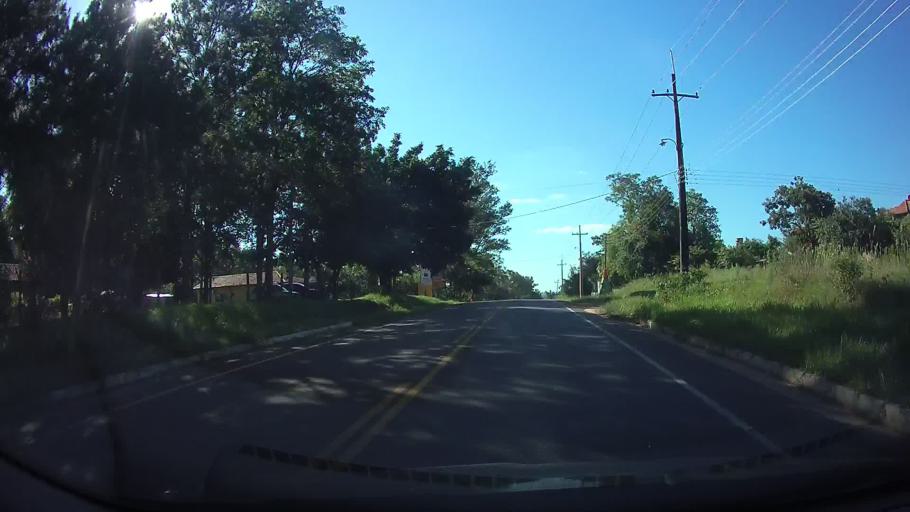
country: PY
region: Cordillera
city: Atyra
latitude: -25.3106
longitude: -57.1507
